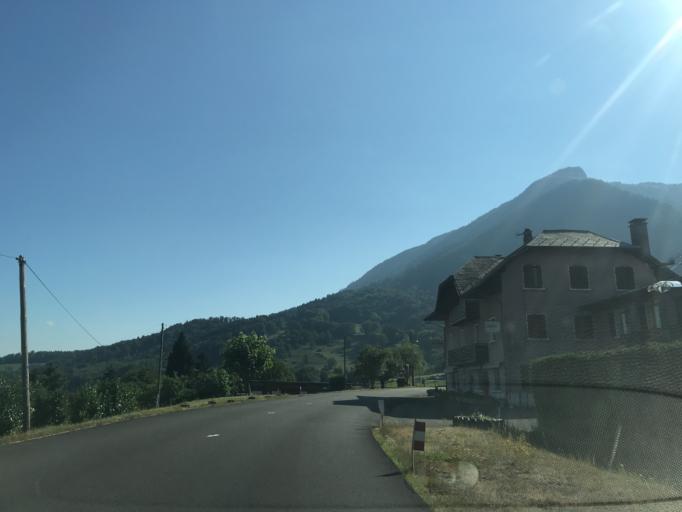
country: FR
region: Rhone-Alpes
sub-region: Departement de la Haute-Savoie
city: Villaz
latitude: 45.9582
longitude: 6.2091
